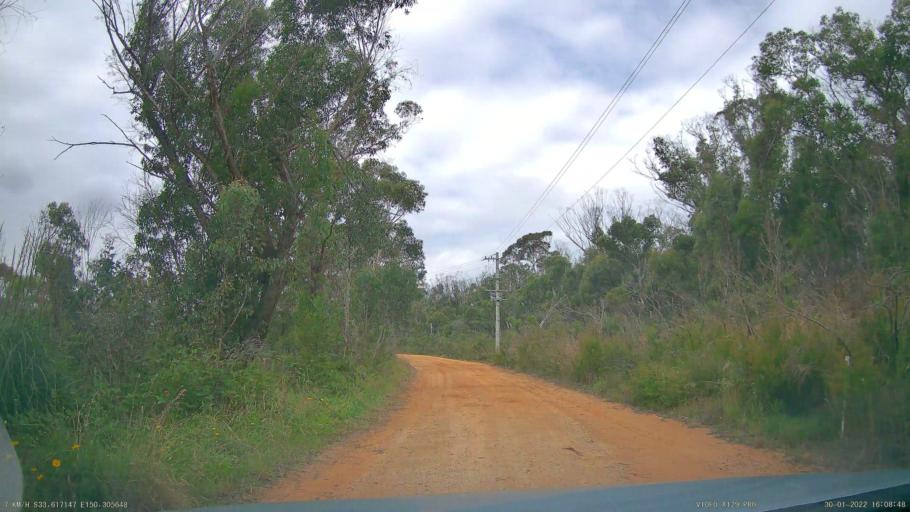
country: AU
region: New South Wales
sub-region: Blue Mountains Municipality
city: Blackheath
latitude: -33.6171
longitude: 150.3057
